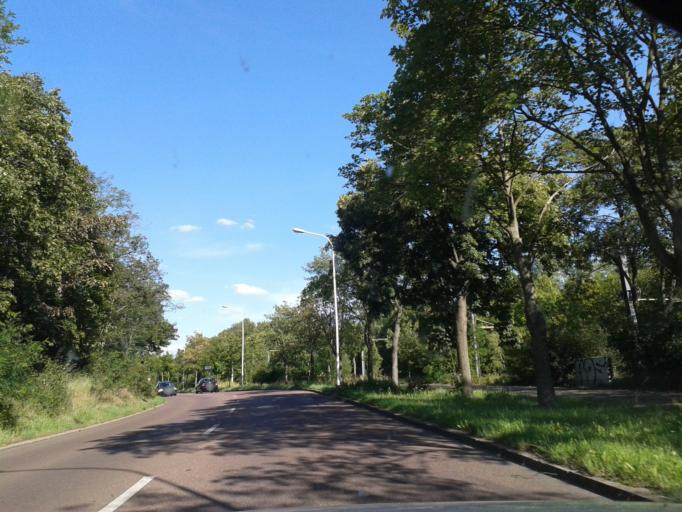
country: DE
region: Saxony-Anhalt
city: Halle Neustadt
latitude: 51.5080
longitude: 11.9292
